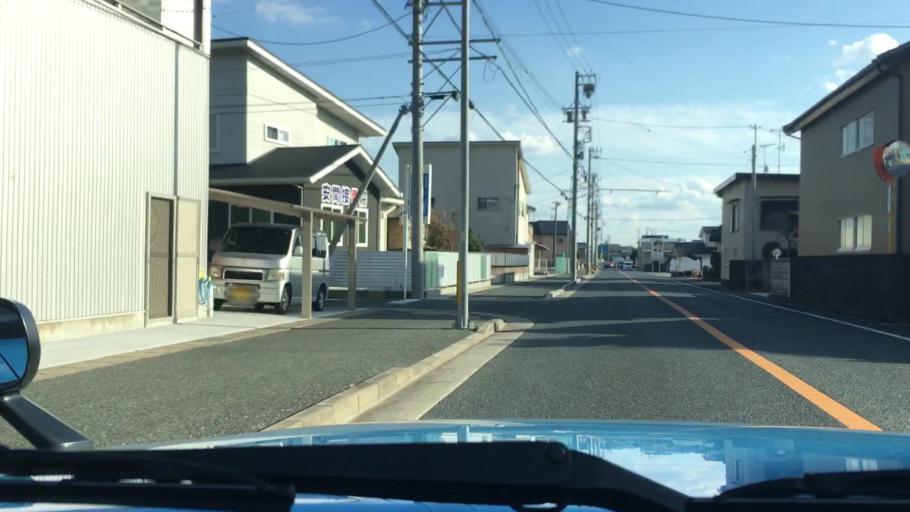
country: JP
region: Shizuoka
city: Hamamatsu
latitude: 34.7546
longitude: 137.6706
